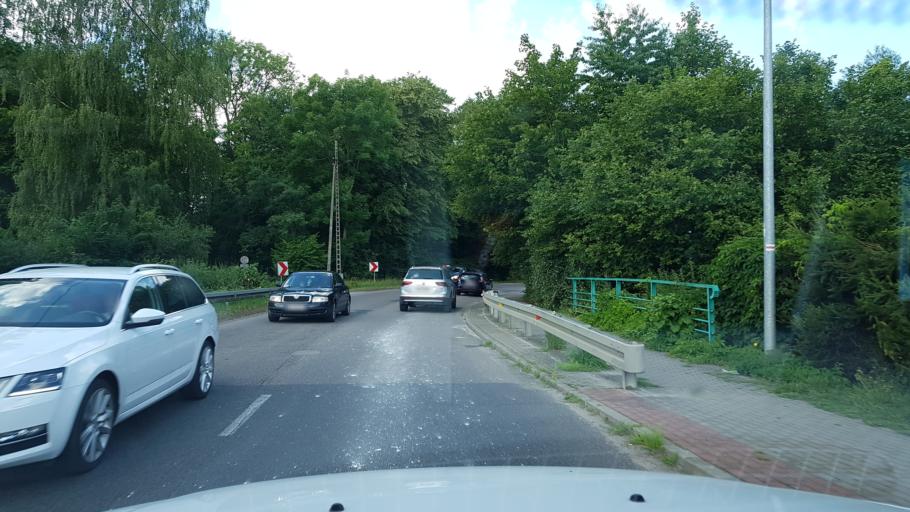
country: PL
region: West Pomeranian Voivodeship
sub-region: Powiat gryficki
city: Trzebiatow
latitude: 54.0639
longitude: 15.2549
